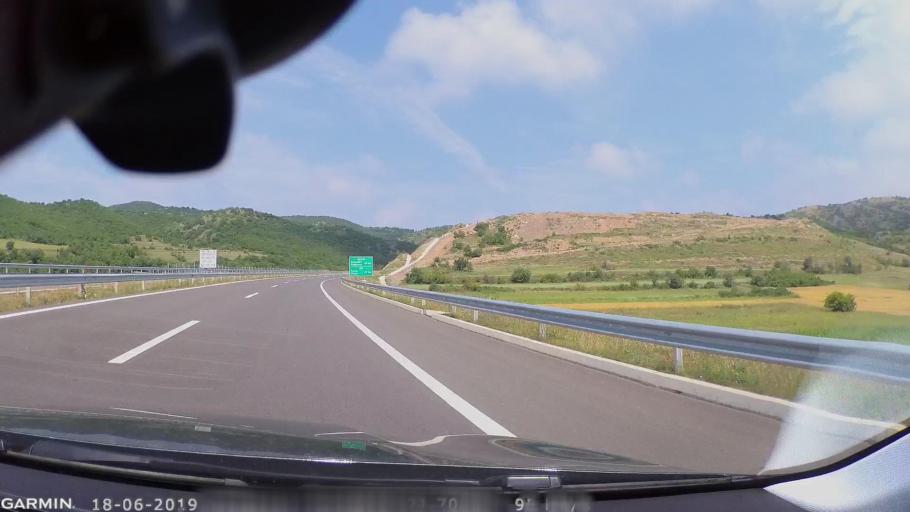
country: MK
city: Miladinovci
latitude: 41.9852
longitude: 21.6560
